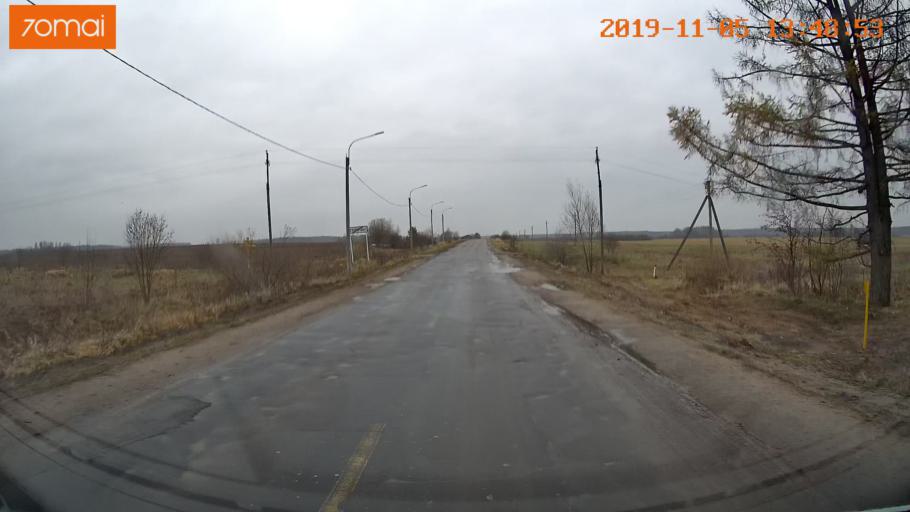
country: RU
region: Ivanovo
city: Shuya
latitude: 57.0058
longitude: 41.4076
